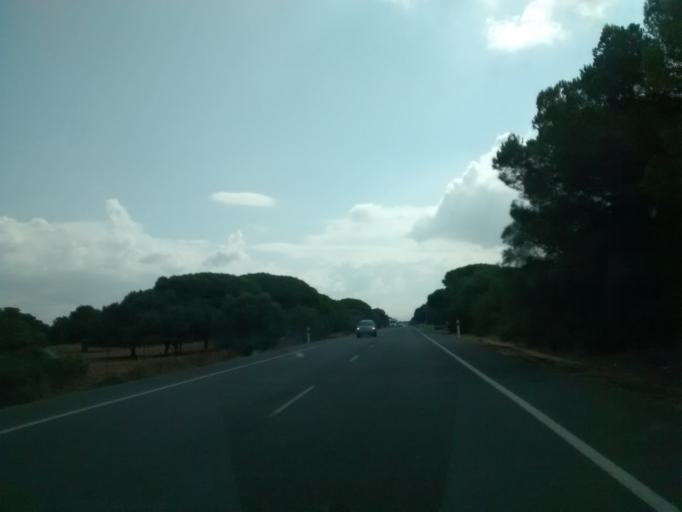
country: ES
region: Andalusia
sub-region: Provincia de Cadiz
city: Barbate de Franco
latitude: 36.2466
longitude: -5.9067
